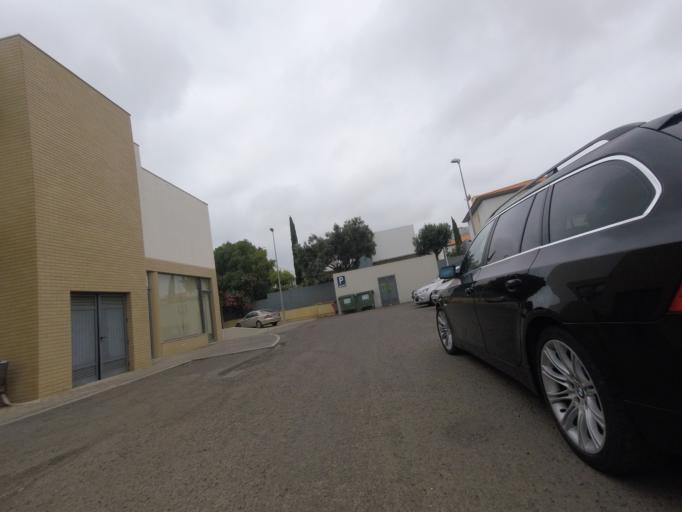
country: PT
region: Madeira
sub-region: Porto Santo
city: Vila de Porto Santo
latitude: 33.0507
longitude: -16.3510
